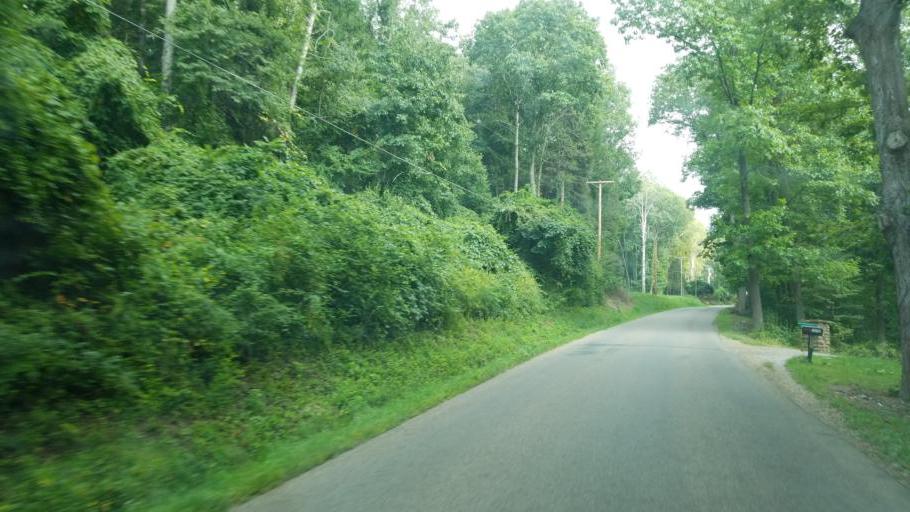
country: US
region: Ohio
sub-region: Knox County
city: Mount Vernon
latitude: 40.3707
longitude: -82.4553
